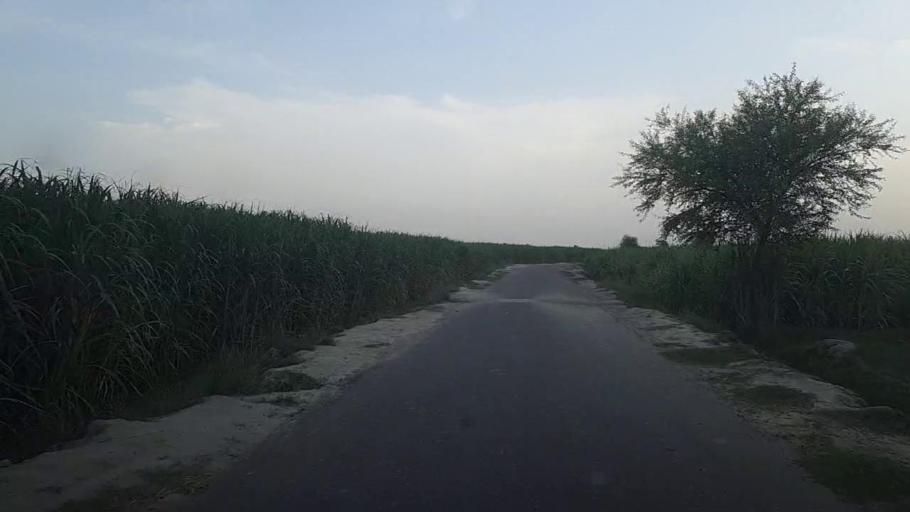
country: PK
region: Sindh
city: Ubauro
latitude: 28.3573
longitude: 69.7842
